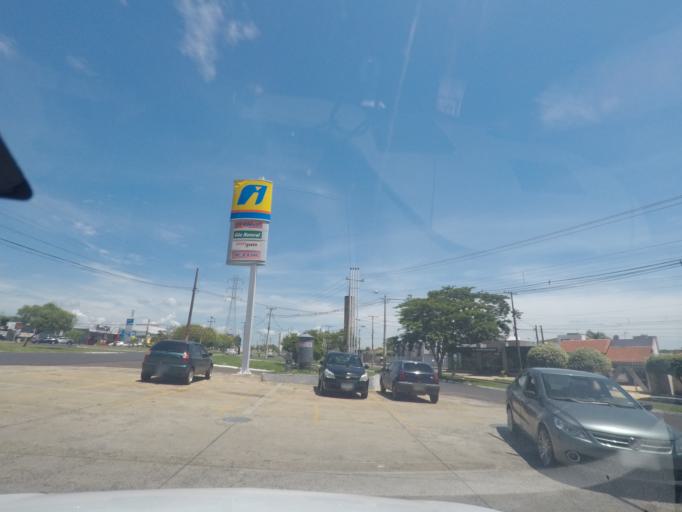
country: BR
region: Sao Paulo
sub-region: Matao
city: Matao
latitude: -21.6120
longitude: -48.3672
